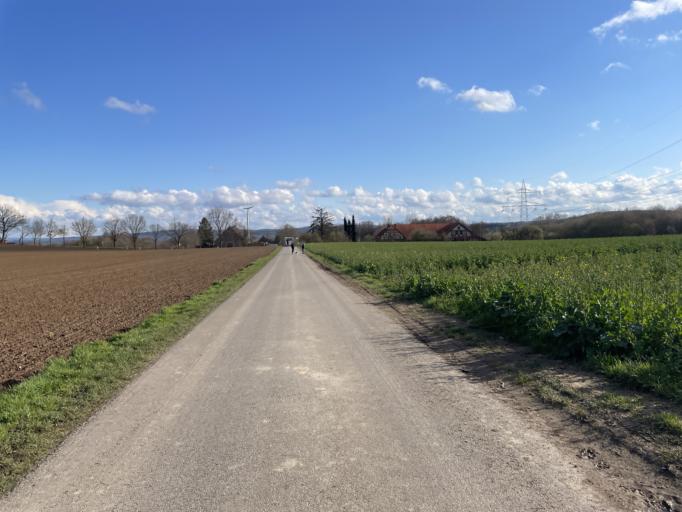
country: DE
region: North Rhine-Westphalia
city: Porta Westfalica
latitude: 52.2229
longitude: 8.9684
